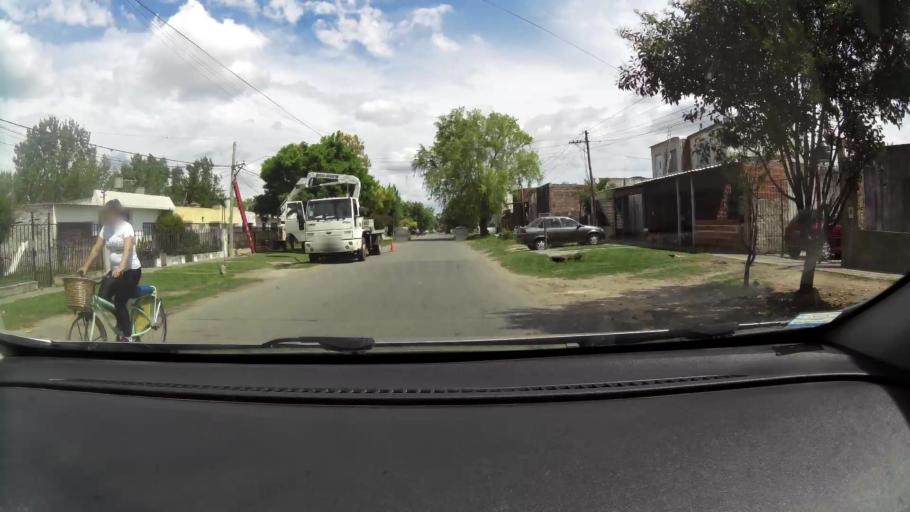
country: AR
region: Santa Fe
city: Gobernador Galvez
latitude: -33.0100
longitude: -60.6422
